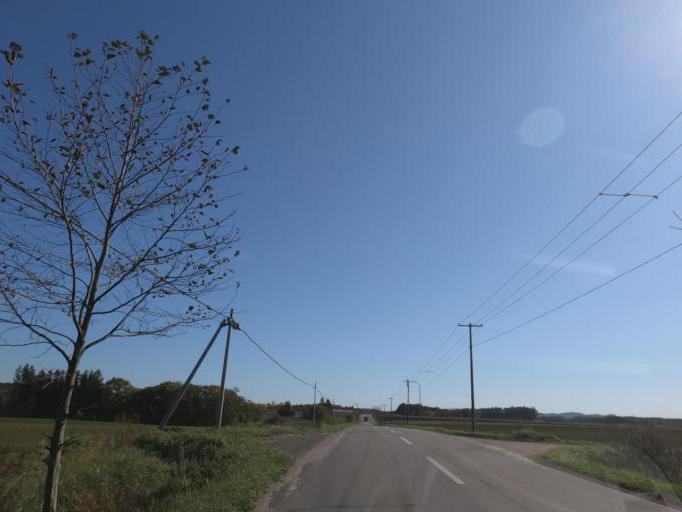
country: JP
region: Hokkaido
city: Obihiro
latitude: 42.8070
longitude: 143.2548
